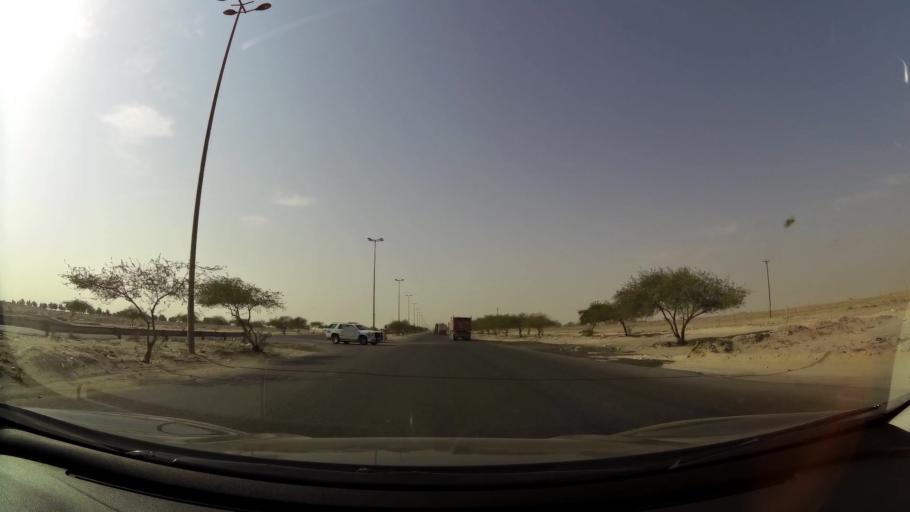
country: KW
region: Al Ahmadi
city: Al Ahmadi
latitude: 28.9422
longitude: 48.1131
